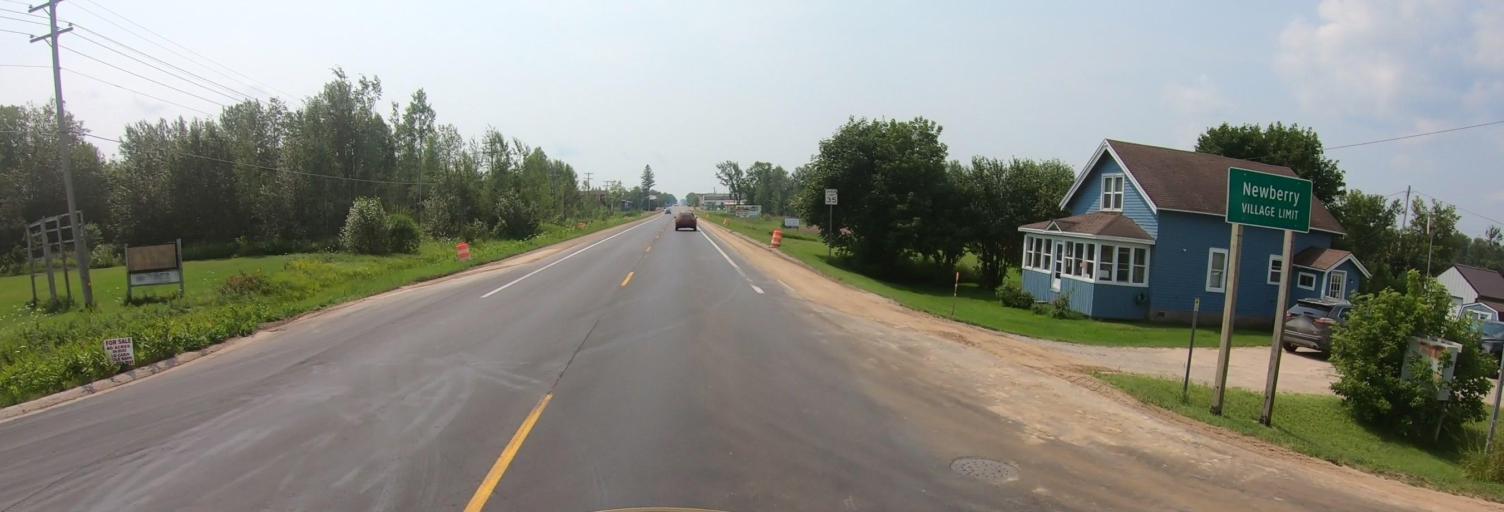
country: US
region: Michigan
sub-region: Luce County
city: Newberry
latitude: 46.3618
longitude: -85.5096
